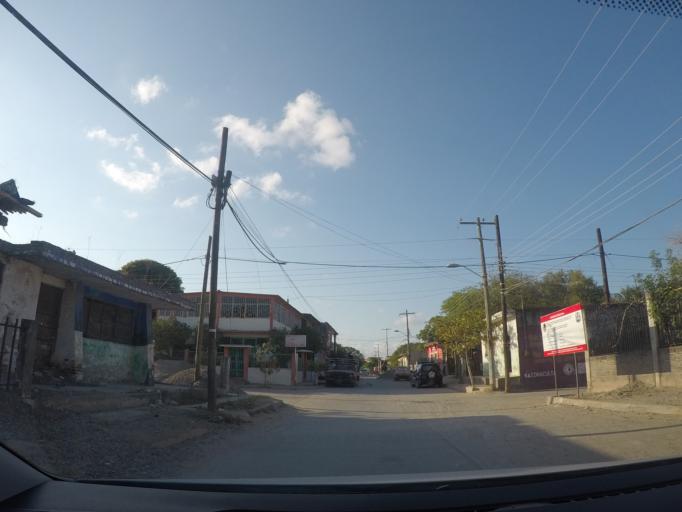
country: MX
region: Oaxaca
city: Juchitan de Zaragoza
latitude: 16.4358
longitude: -95.0267
